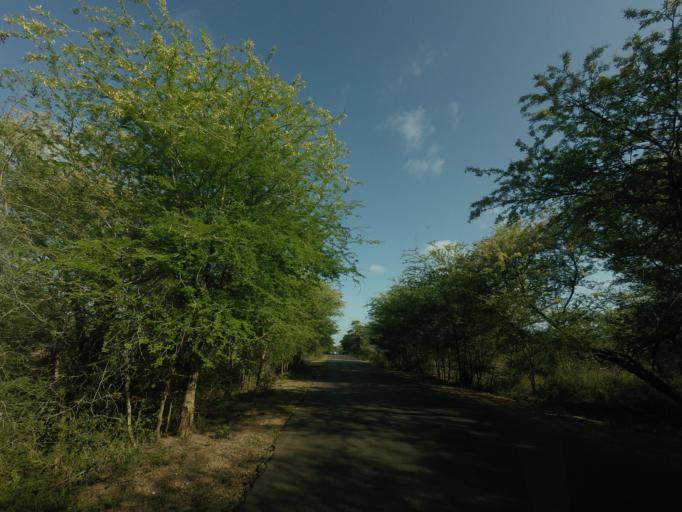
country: ZA
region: Mpumalanga
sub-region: Ehlanzeni District
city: Komatipoort
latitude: -25.2664
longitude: 31.8478
